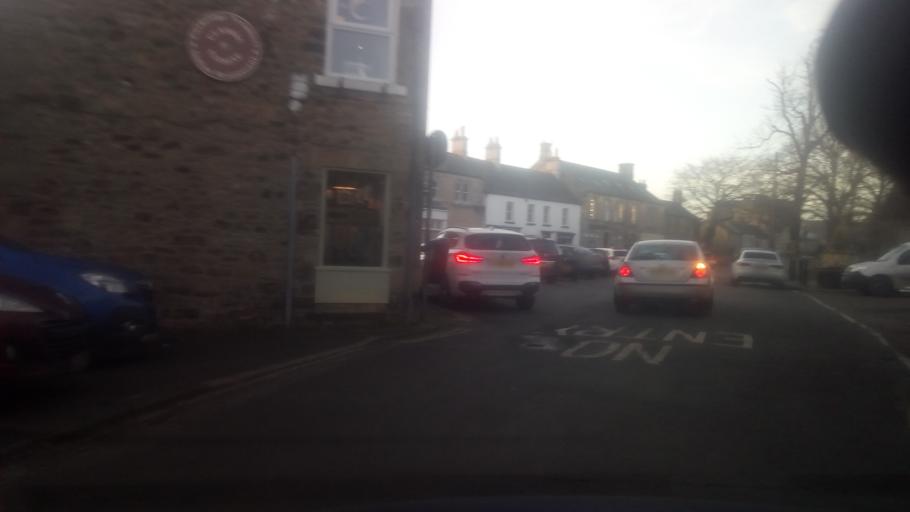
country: GB
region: England
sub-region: Northumberland
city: Corbridge
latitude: 54.9738
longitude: -2.0197
